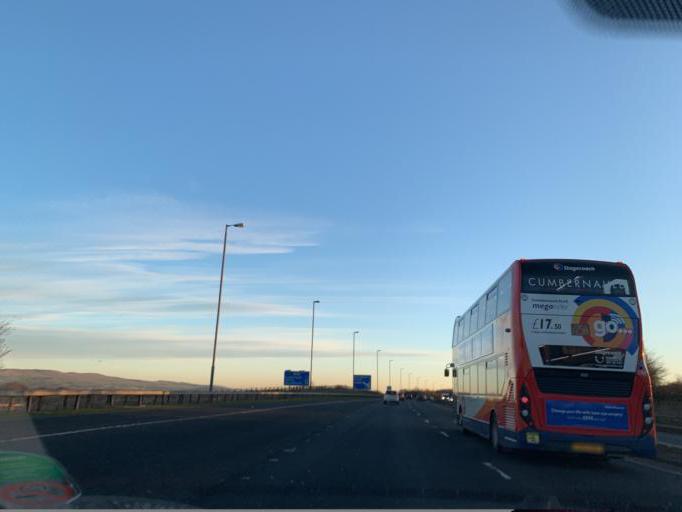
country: GB
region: Scotland
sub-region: North Lanarkshire
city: Stepps
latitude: 55.8927
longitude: -4.1734
